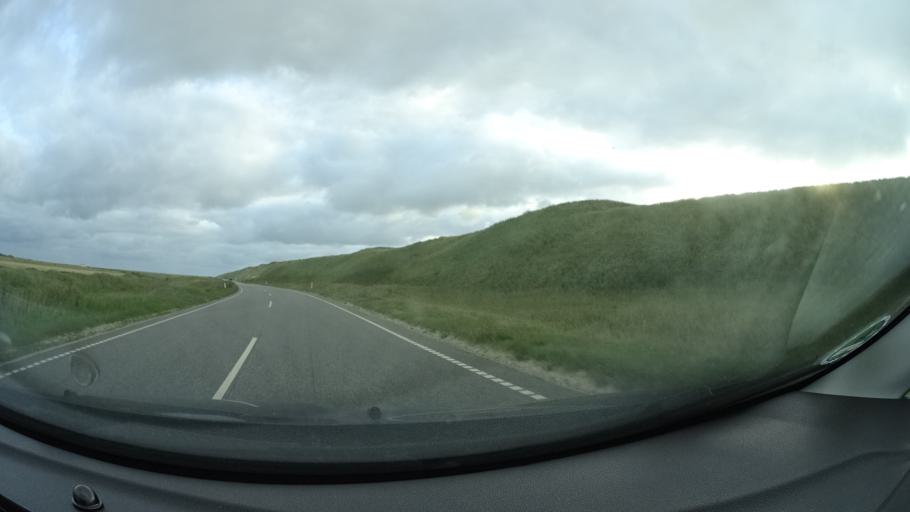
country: DK
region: Central Jutland
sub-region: Lemvig Kommune
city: Harboore
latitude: 56.4519
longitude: 8.1259
